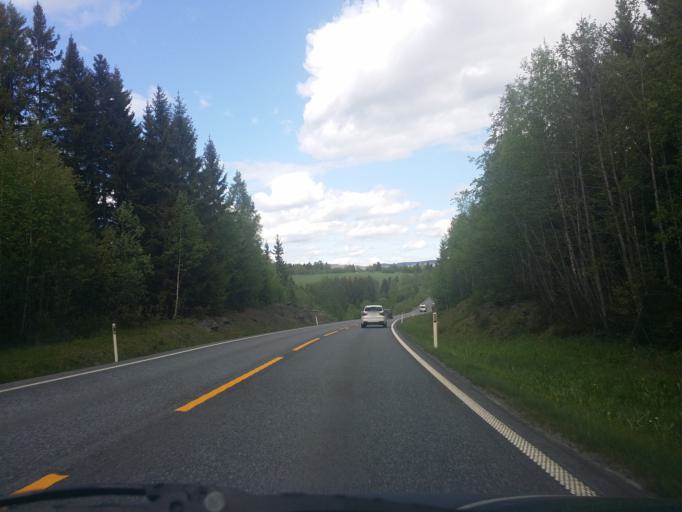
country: NO
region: Oppland
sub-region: Lunner
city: Roa
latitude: 60.2869
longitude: 10.5448
